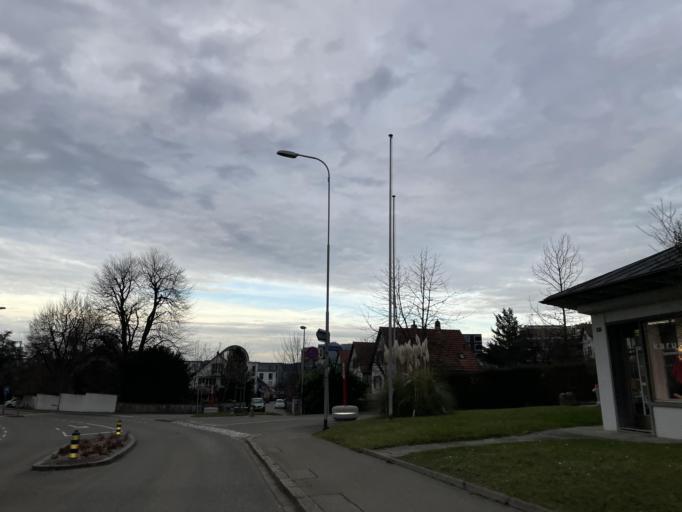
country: CH
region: Zurich
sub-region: Bezirk Buelach
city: Kloten / Ruetlen
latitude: 47.4470
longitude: 8.5866
